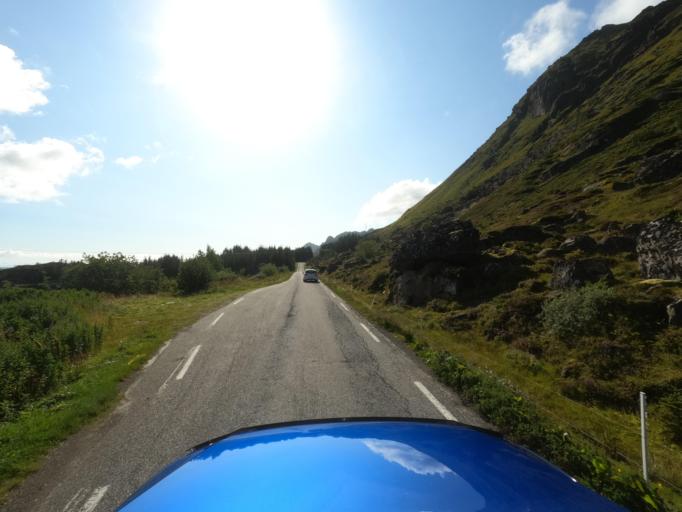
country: NO
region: Nordland
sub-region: Vestvagoy
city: Leknes
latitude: 68.1253
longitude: 13.7410
